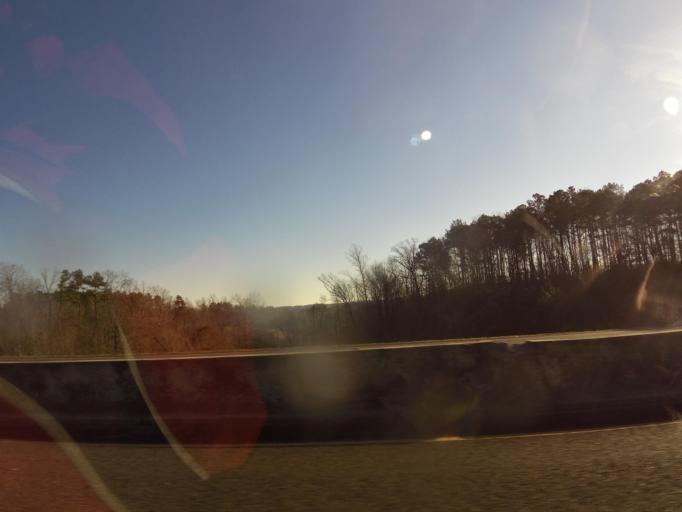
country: US
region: Alabama
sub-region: Blount County
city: Smoke Rise
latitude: 33.9245
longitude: -86.8670
